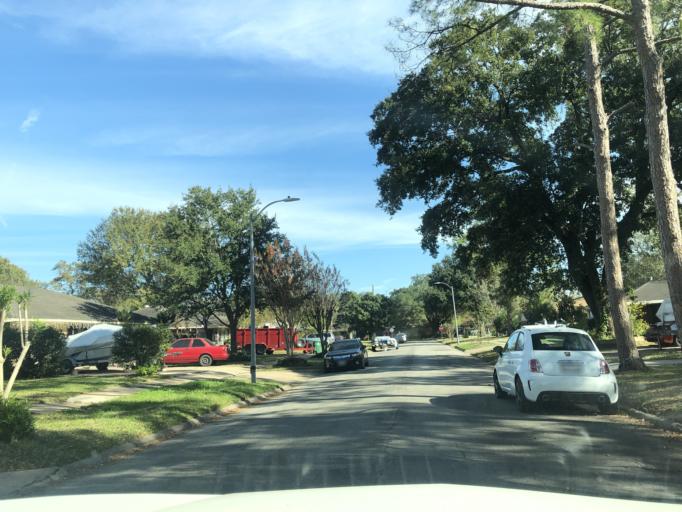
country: US
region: Texas
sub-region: Harris County
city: Bellaire
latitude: 29.6831
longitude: -95.5072
